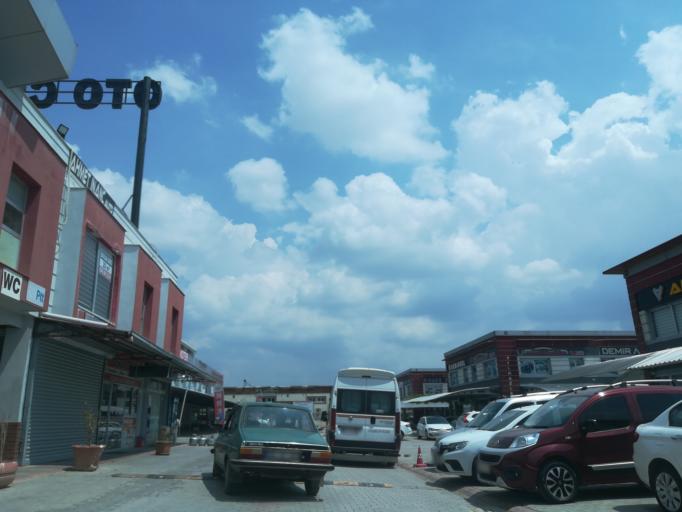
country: TR
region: Adana
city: Seyhan
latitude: 37.0020
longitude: 35.2453
